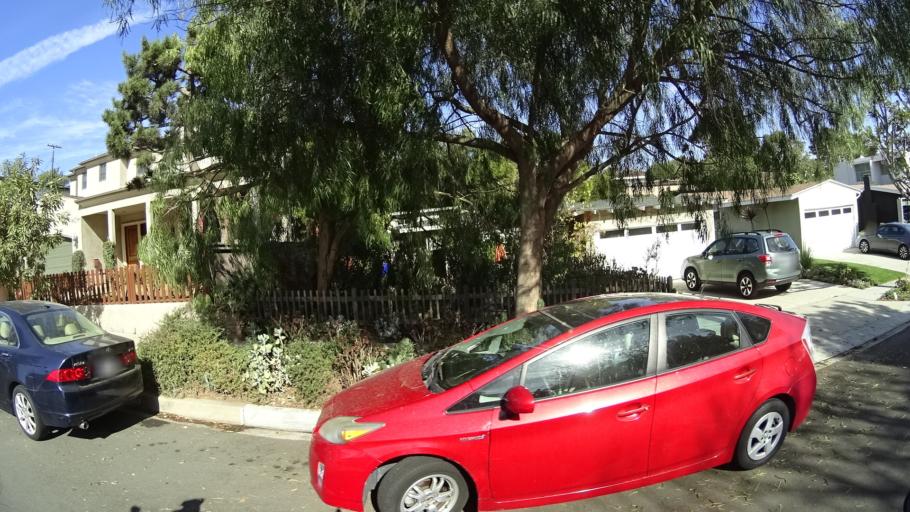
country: US
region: California
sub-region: Los Angeles County
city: Hermosa Beach
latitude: 33.8772
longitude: -118.3905
